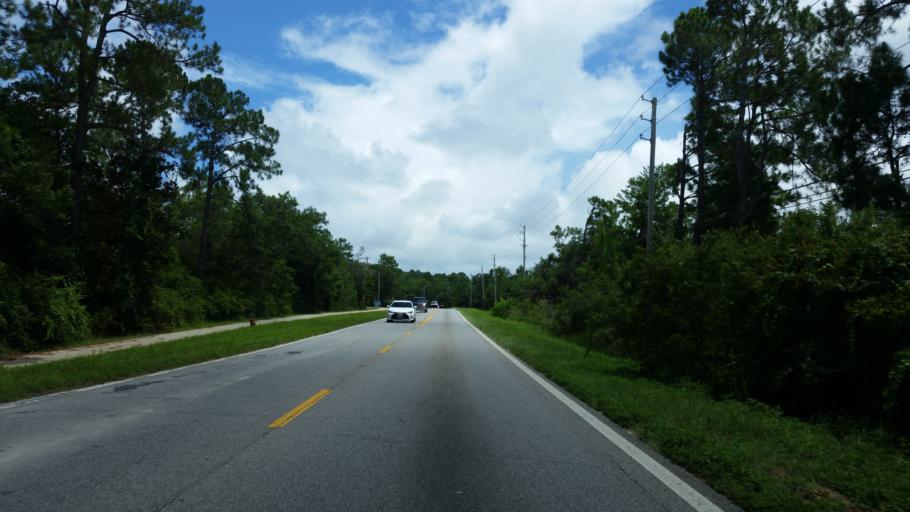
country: US
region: Florida
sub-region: Santa Rosa County
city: Holley
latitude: 30.4376
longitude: -86.9184
